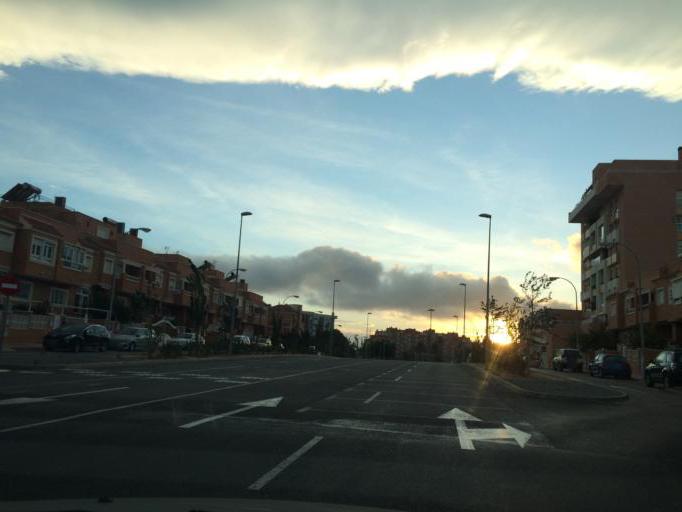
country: ES
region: Andalusia
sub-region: Provincia de Almeria
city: Almeria
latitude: 36.8578
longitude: -2.4430
